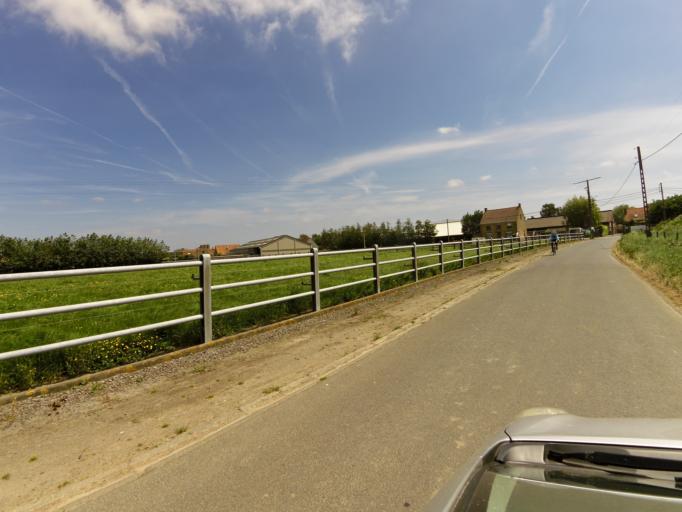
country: BE
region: Flanders
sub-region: Provincie West-Vlaanderen
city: Diksmuide
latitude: 50.9971
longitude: 2.8613
